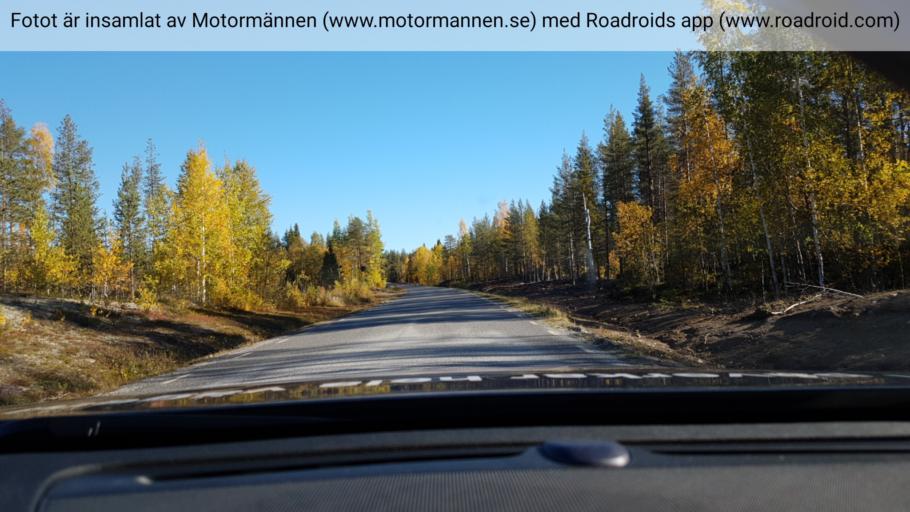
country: SE
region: Norrbotten
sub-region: Gallivare Kommun
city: Gaellivare
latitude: 66.4670
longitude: 20.8296
